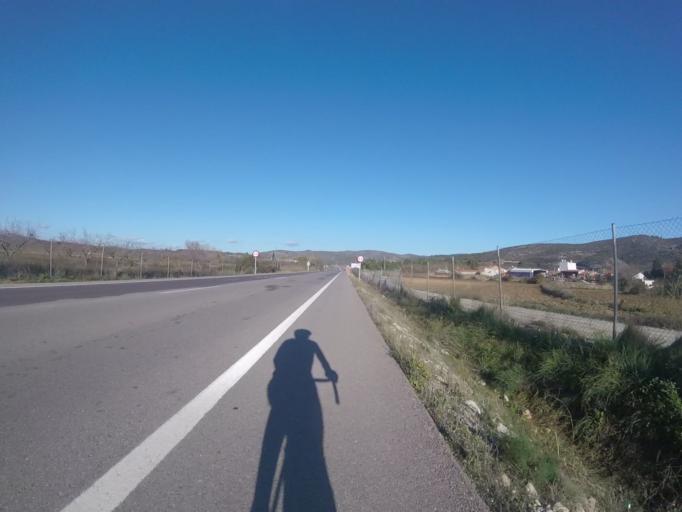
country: ES
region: Valencia
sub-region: Provincia de Castello
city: Cuevas de Vinroma
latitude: 40.3146
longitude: 0.1201
